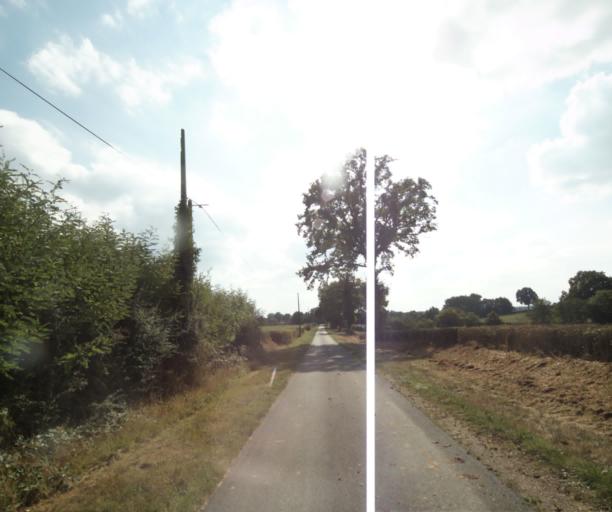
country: FR
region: Bourgogne
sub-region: Departement de Saone-et-Loire
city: Palinges
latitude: 46.5050
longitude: 4.2235
